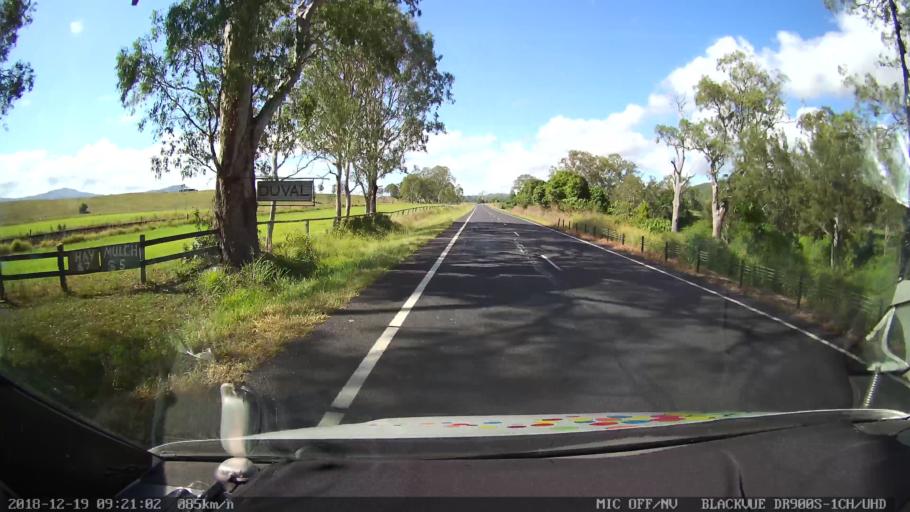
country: AU
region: New South Wales
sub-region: Kyogle
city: Kyogle
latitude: -28.5787
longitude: 152.9824
